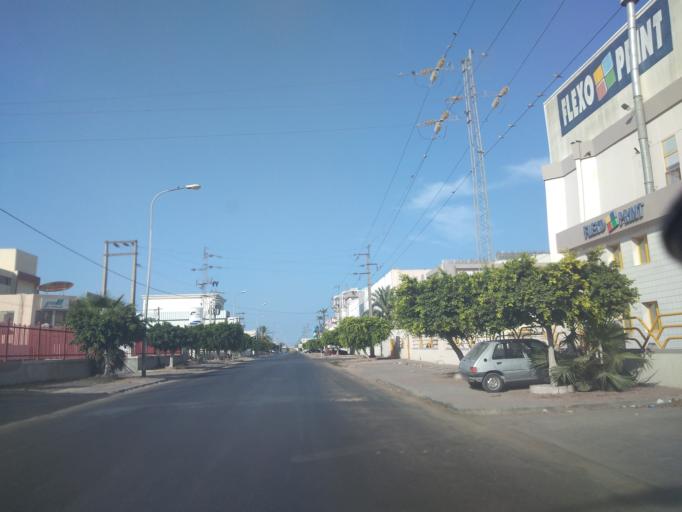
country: TN
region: Safaqis
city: Sfax
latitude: 34.7458
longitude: 10.7696
